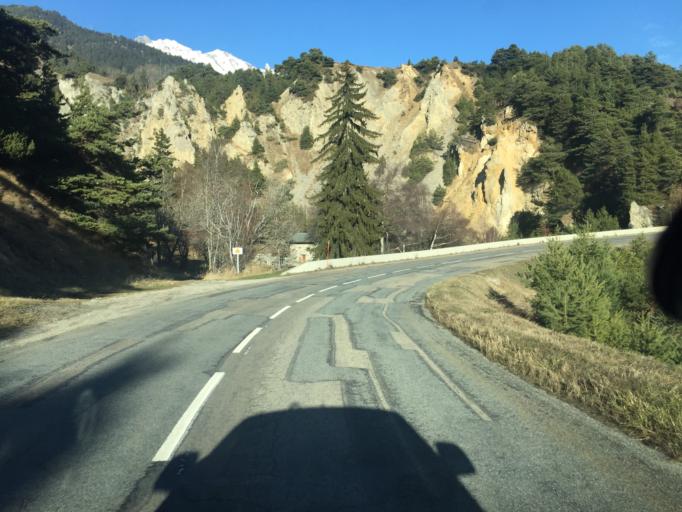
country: FR
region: Rhone-Alpes
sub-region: Departement de la Savoie
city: Modane
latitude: 45.2266
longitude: 6.7337
